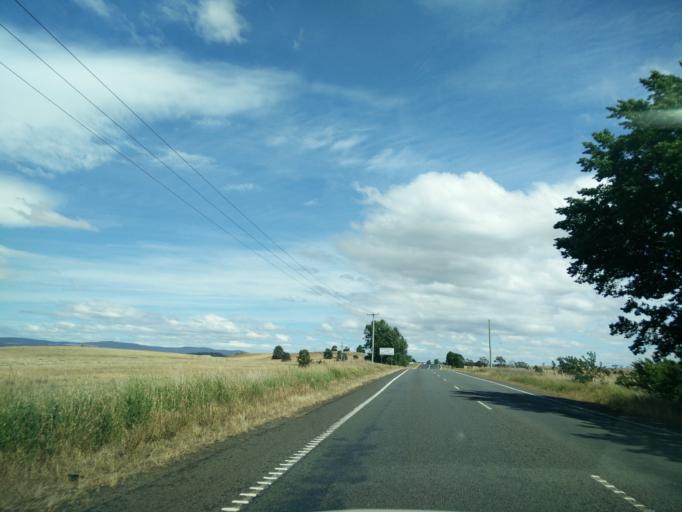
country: AU
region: Tasmania
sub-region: Northern Midlands
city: Evandale
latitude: -41.8643
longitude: 147.4573
